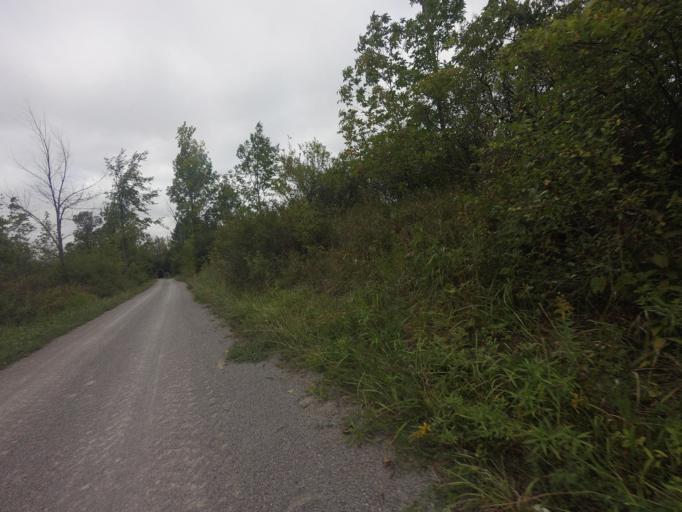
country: CA
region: Ontario
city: Omemee
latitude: 44.4285
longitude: -78.7693
